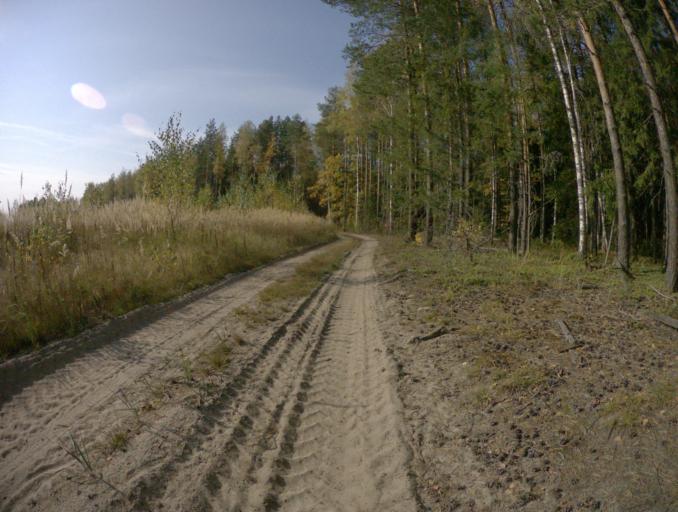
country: RU
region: Vladimir
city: Vorsha
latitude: 55.9554
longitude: 40.1445
